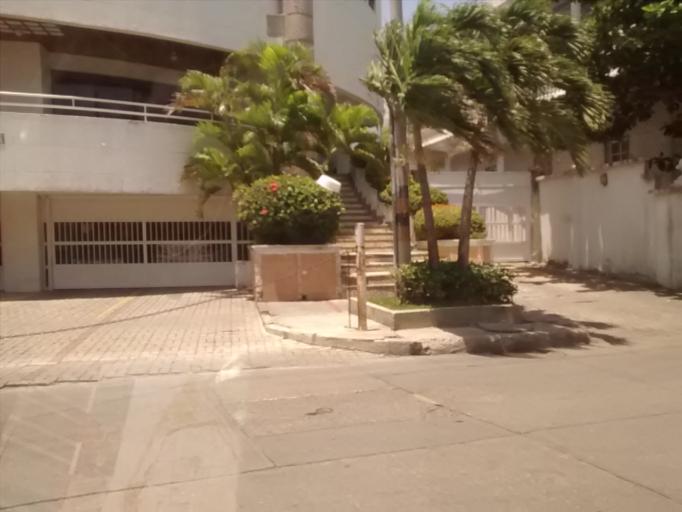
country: CO
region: Bolivar
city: Cartagena
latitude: 10.4165
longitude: -75.5420
